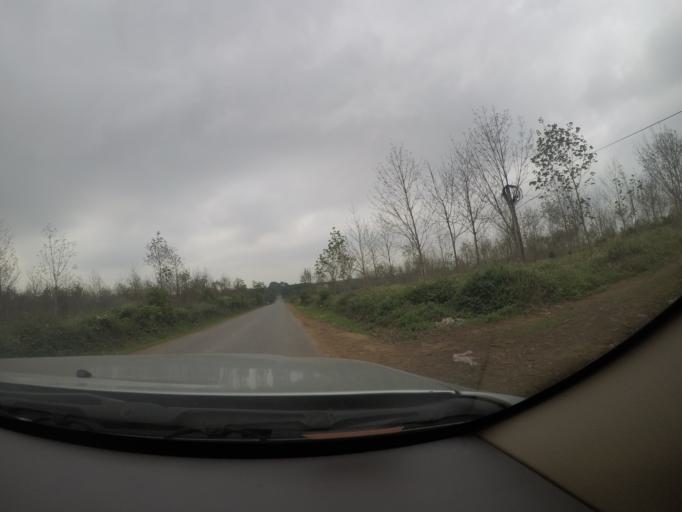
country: VN
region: Quang Binh
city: Ba Don
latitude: 17.6422
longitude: 106.4344
